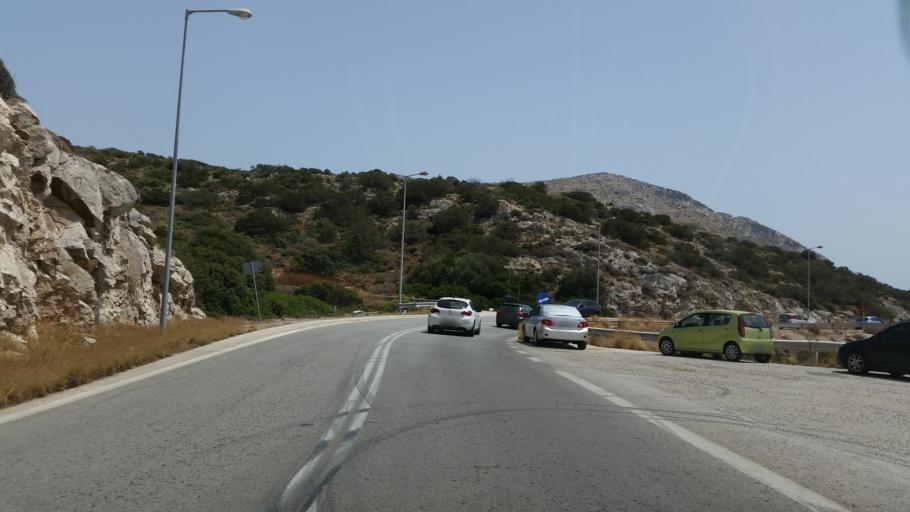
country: GR
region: Attica
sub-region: Nomarchia Anatolikis Attikis
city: Palaia Fokaia
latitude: 37.6851
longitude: 23.9384
